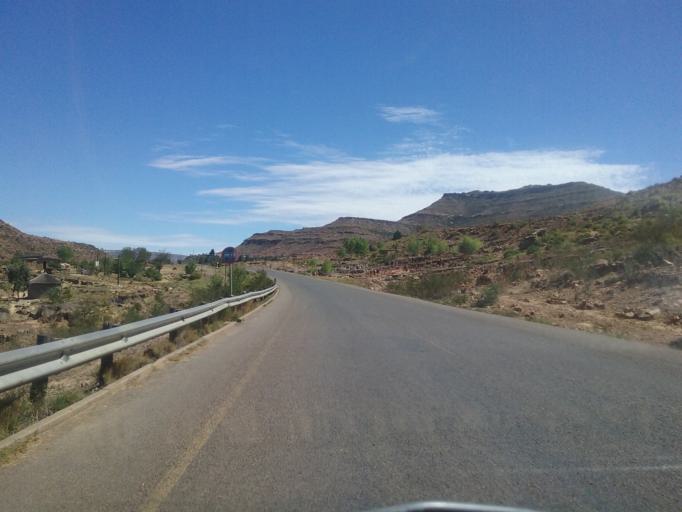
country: LS
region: Quthing
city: Quthing
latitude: -30.3518
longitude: 27.5450
